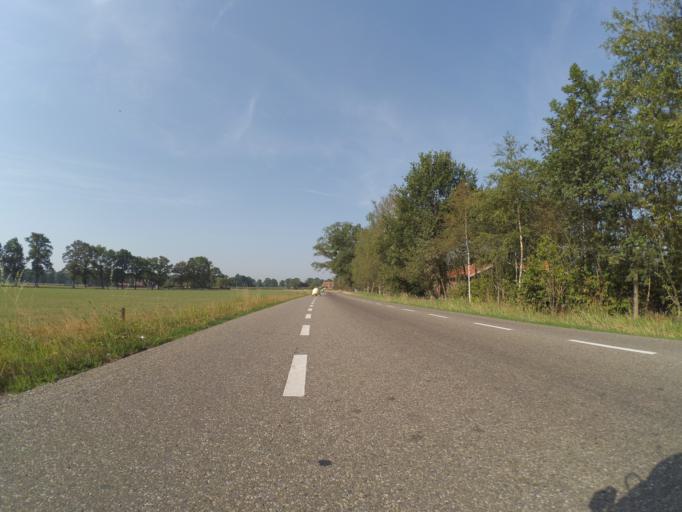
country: NL
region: Overijssel
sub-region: Gemeente Tubbergen
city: Tubbergen
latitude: 52.3801
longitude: 6.8531
